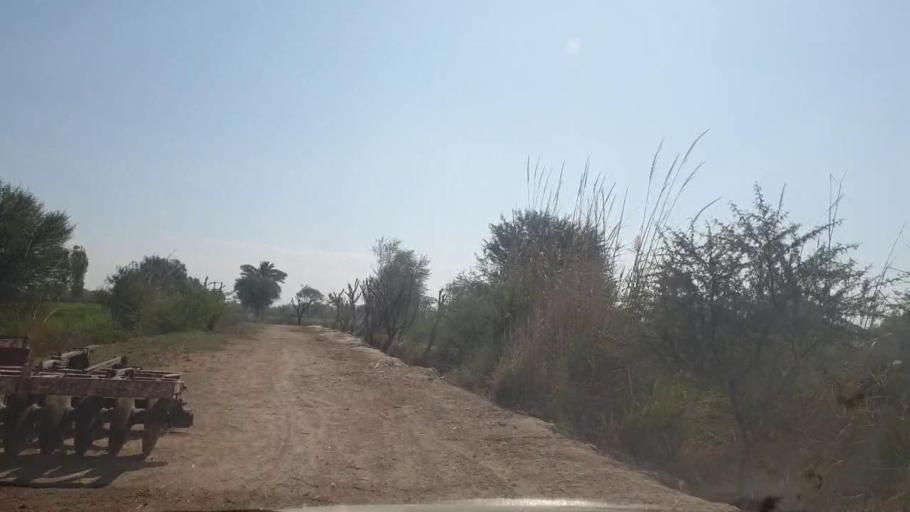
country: PK
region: Sindh
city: Mirpur Khas
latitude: 25.5184
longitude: 69.1622
